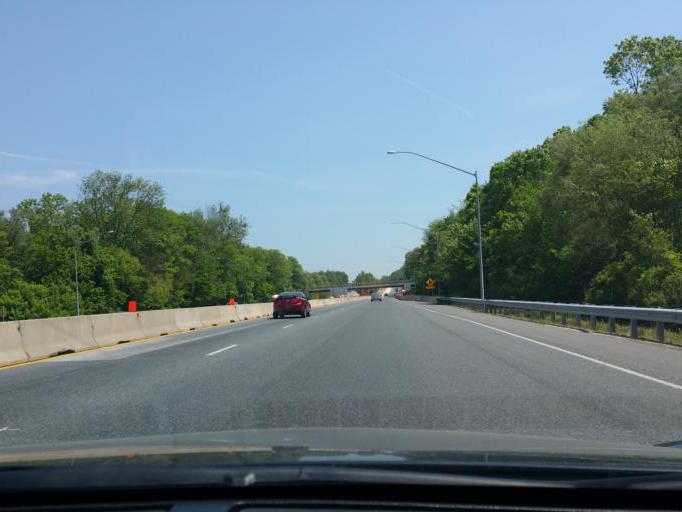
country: US
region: Maryland
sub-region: Howard County
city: Columbia
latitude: 39.2070
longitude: -76.8563
